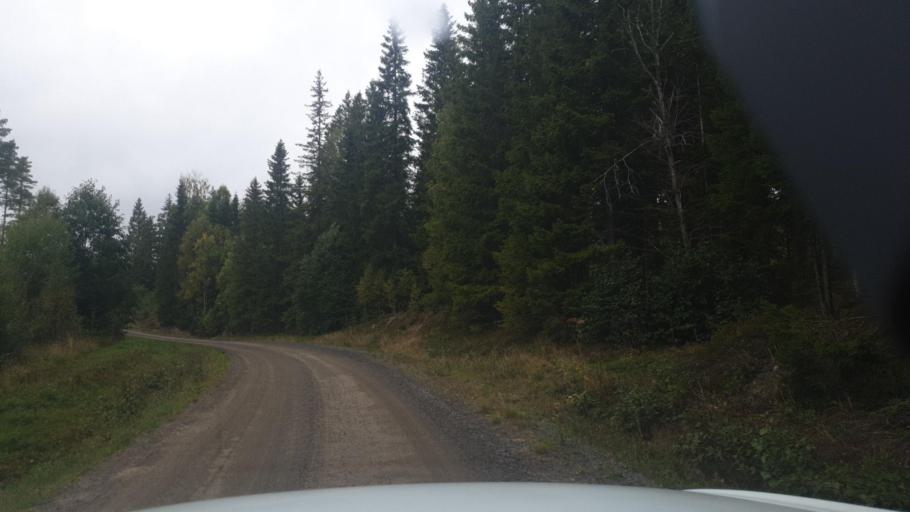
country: SE
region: Vaermland
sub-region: Sunne Kommun
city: Sunne
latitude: 59.8616
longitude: 12.8347
